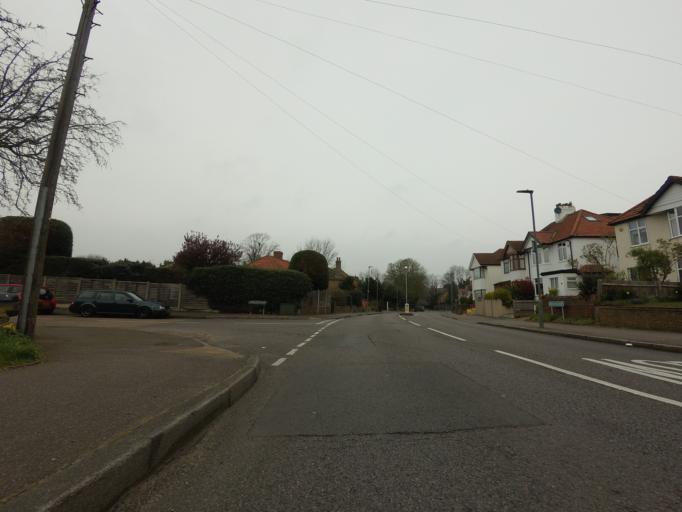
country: GB
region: England
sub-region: Greater London
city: Orpington
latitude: 51.3846
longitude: 0.1146
